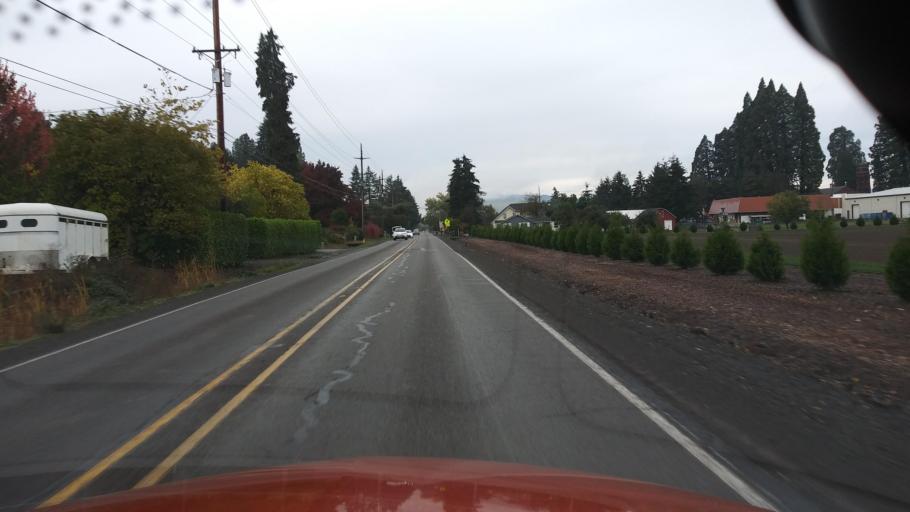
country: US
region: Oregon
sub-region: Washington County
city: Cornelius
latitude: 45.5505
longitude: -123.0813
